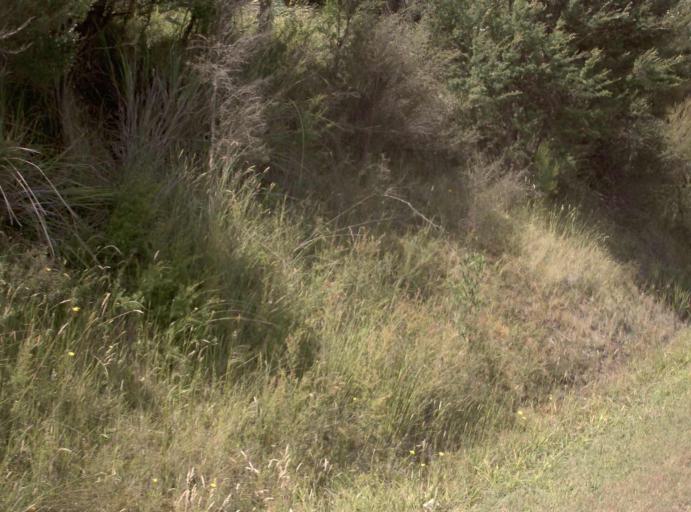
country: AU
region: Victoria
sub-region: Latrobe
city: Morwell
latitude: -38.1614
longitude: 146.3838
